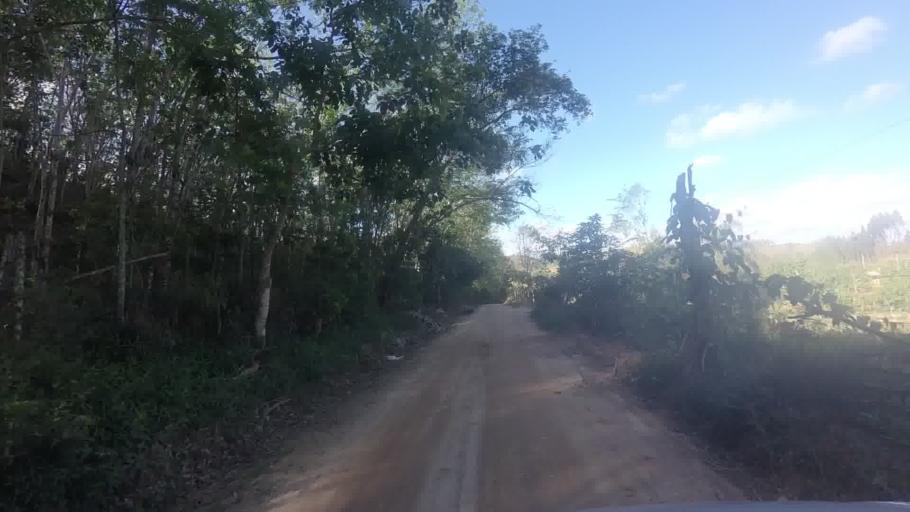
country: BR
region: Espirito Santo
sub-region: Sao Jose Do Calcado
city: Sao Jose do Calcado
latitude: -21.0242
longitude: -41.5713
